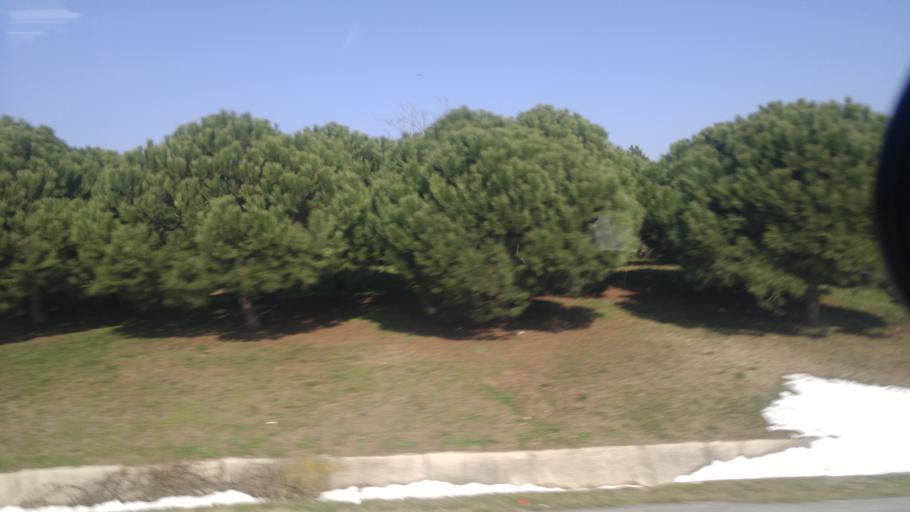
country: TR
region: Istanbul
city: Selimpasa
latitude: 41.0691
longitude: 28.3863
